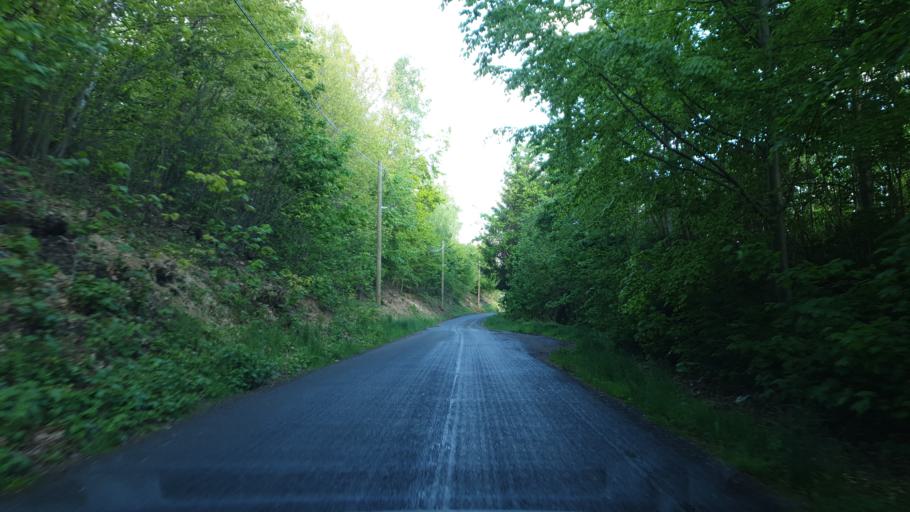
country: DE
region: Saxony
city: Oelsnitz
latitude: 50.7305
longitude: 12.7060
